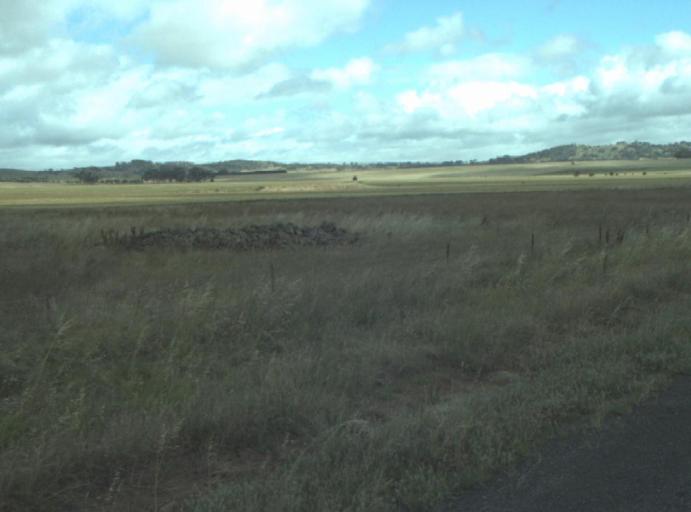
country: AU
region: Victoria
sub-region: Greater Geelong
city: Lara
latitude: -37.9095
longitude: 144.3158
